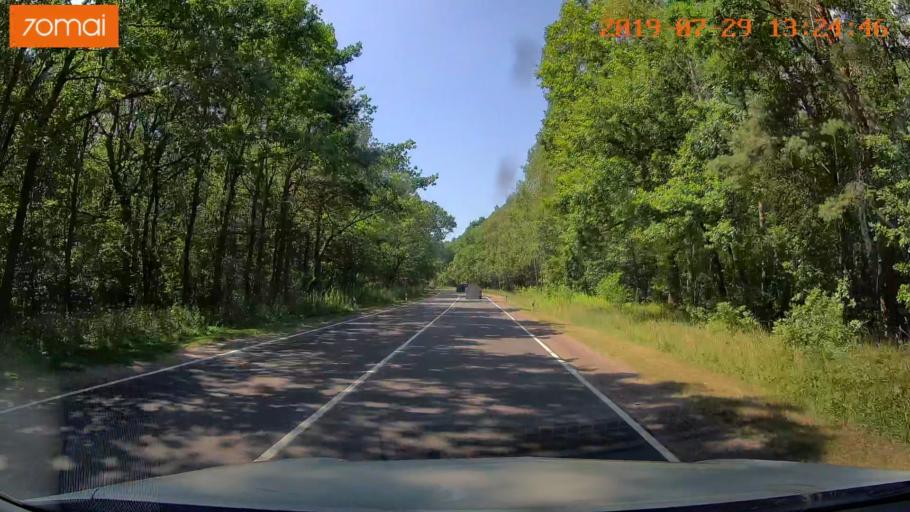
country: RU
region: Kaliningrad
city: Vzmorye
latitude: 54.7126
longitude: 20.3423
